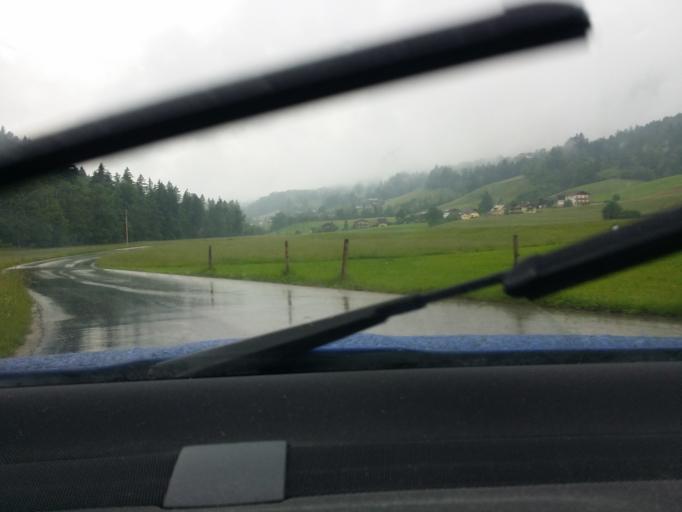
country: AT
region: Salzburg
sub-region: Politischer Bezirk Hallein
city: Abtenau
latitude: 47.5921
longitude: 13.3321
